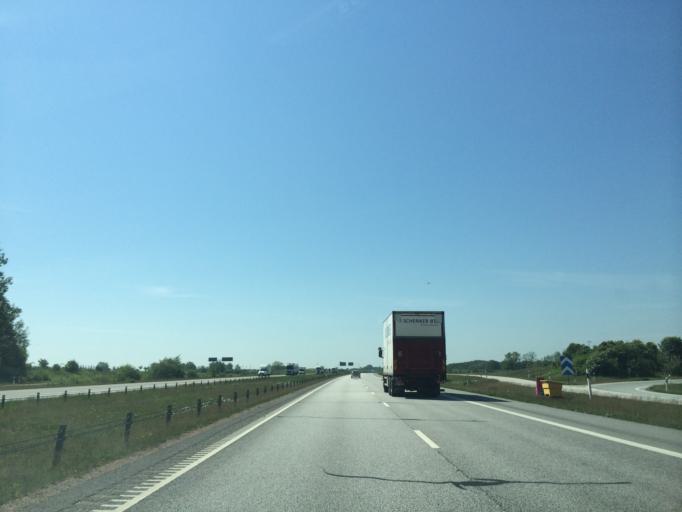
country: SE
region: Skane
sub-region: Malmo
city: Oxie
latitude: 55.5597
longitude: 13.0776
